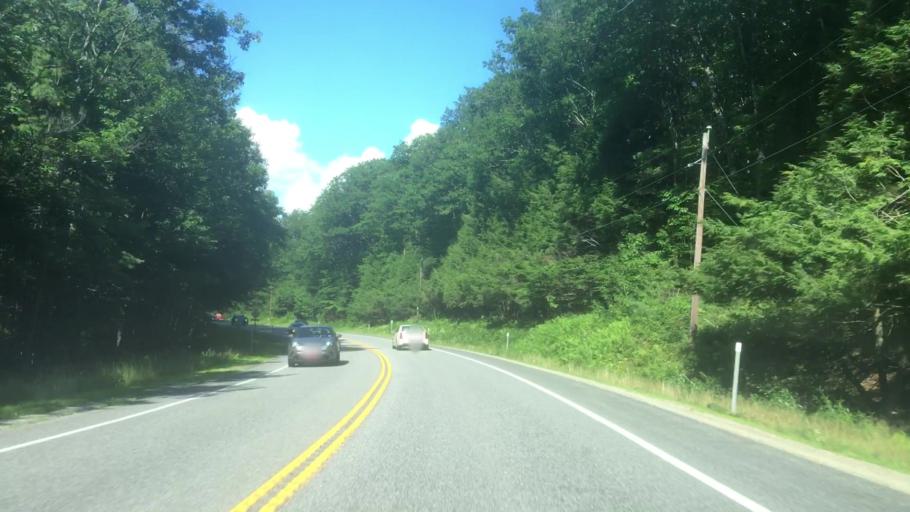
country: US
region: New Hampshire
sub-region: Hillsborough County
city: Antrim
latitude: 43.0673
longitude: -72.0271
